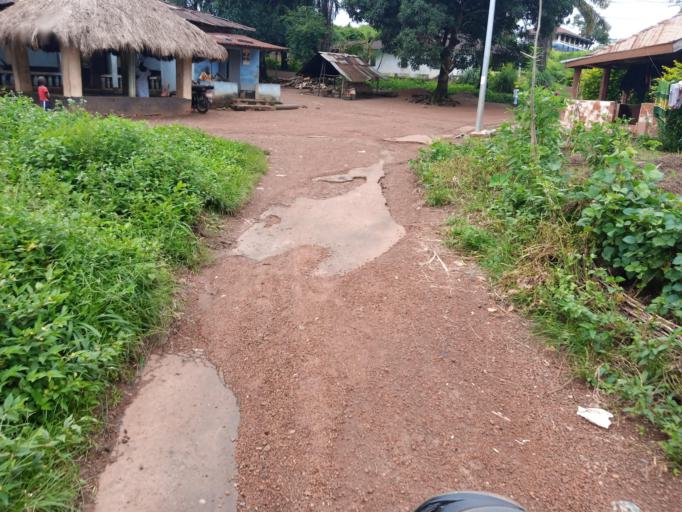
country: SL
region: Southern Province
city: Largo
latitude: 8.2038
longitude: -12.0626
